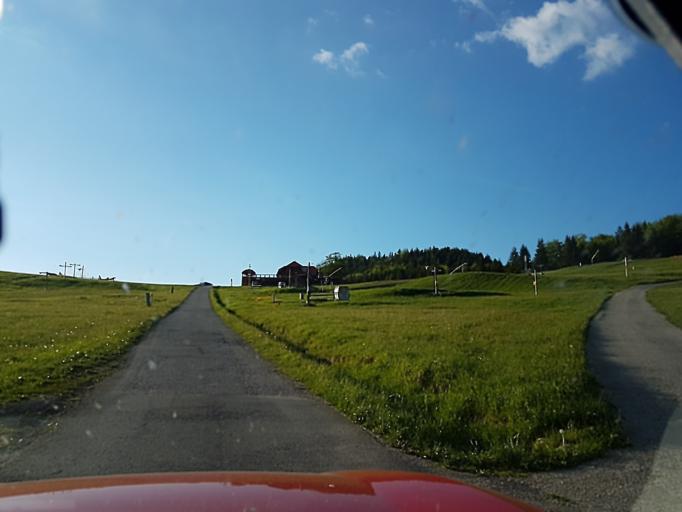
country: SK
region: Zilinsky
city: Ruzomberok
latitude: 49.0518
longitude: 19.2648
